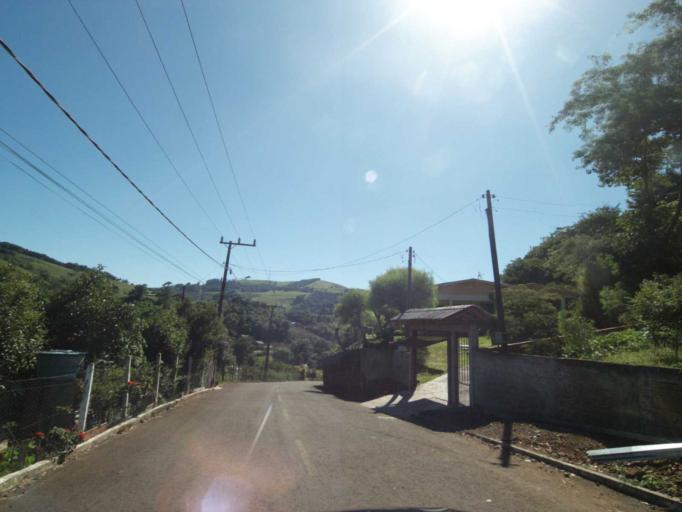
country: BR
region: Parana
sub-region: Francisco Beltrao
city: Francisco Beltrao
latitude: -26.1441
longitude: -53.3099
